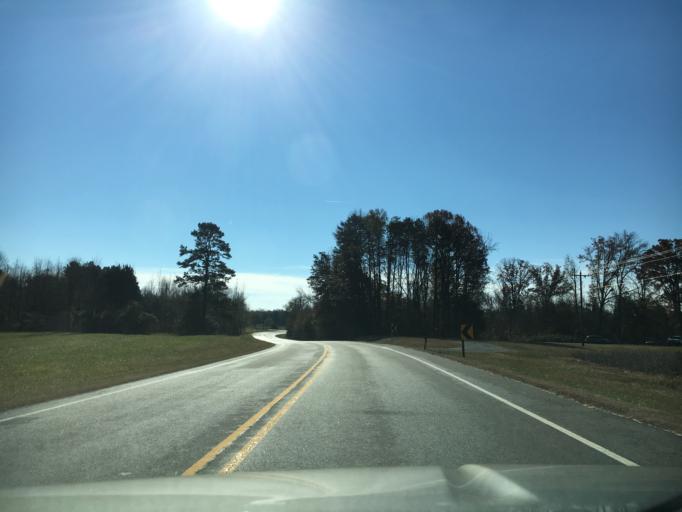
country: US
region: Virginia
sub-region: Cumberland County
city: Cumberland
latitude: 37.5596
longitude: -78.1854
